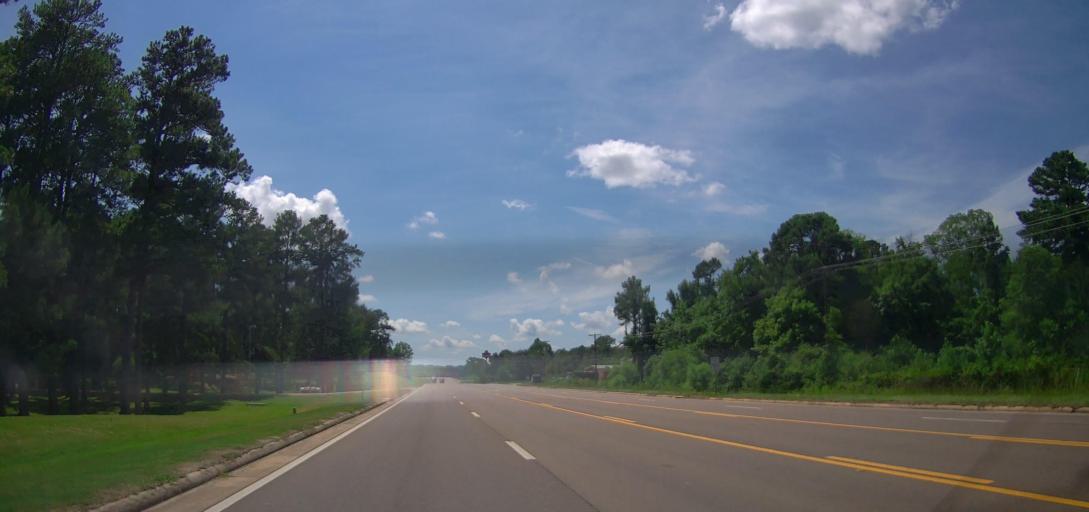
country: US
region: Mississippi
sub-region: Monroe County
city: Aberdeen
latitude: 33.8149
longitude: -88.5584
